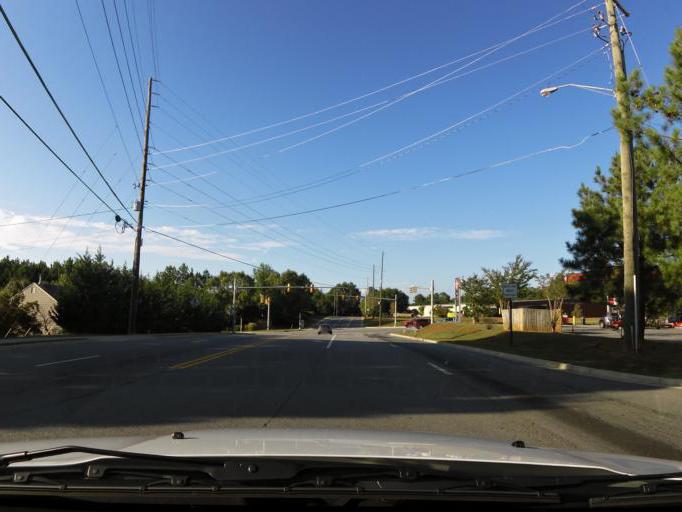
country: US
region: Georgia
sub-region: Cobb County
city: Kennesaw
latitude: 34.0477
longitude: -84.6160
